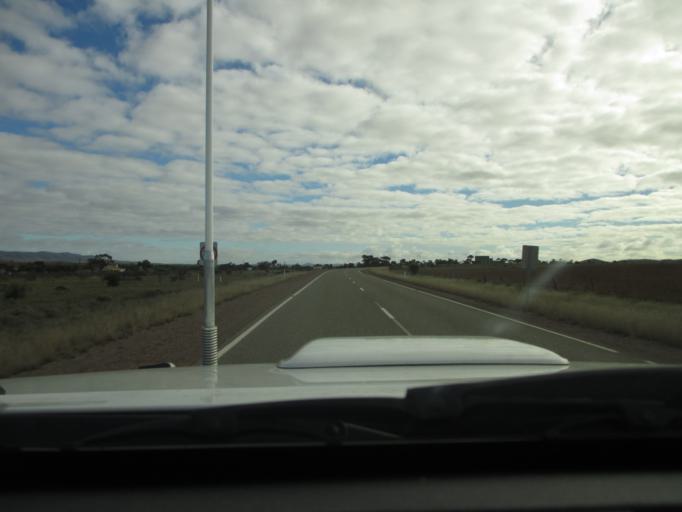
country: AU
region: South Australia
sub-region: Flinders Ranges
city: Quorn
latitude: -32.4317
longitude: 138.5322
